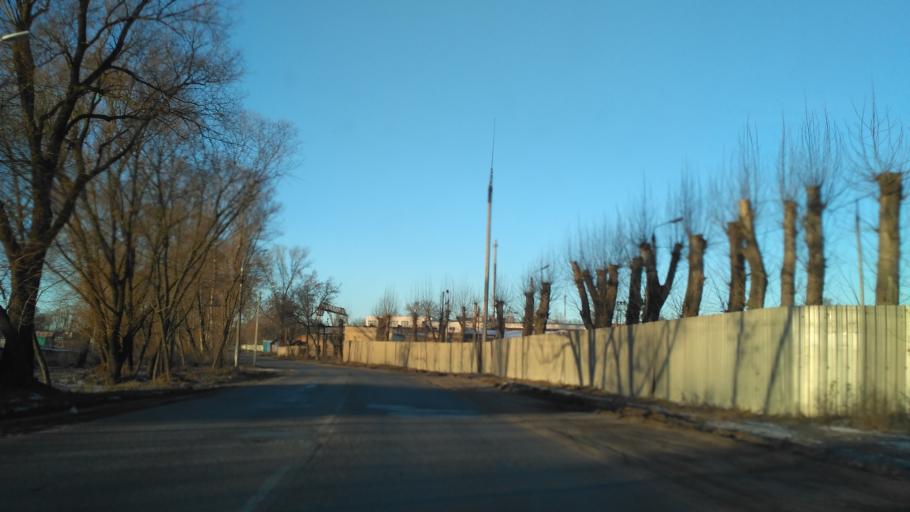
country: RU
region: Tula
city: Tula
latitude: 54.2191
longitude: 37.5923
